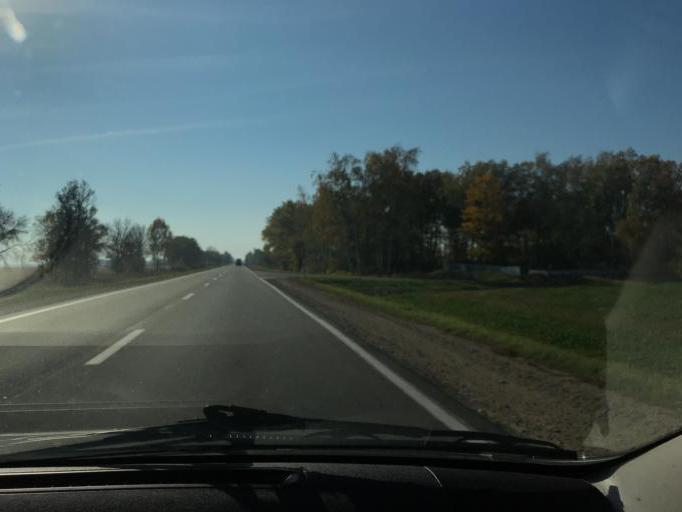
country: BY
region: Minsk
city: Salihorsk
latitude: 52.9096
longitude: 27.4791
